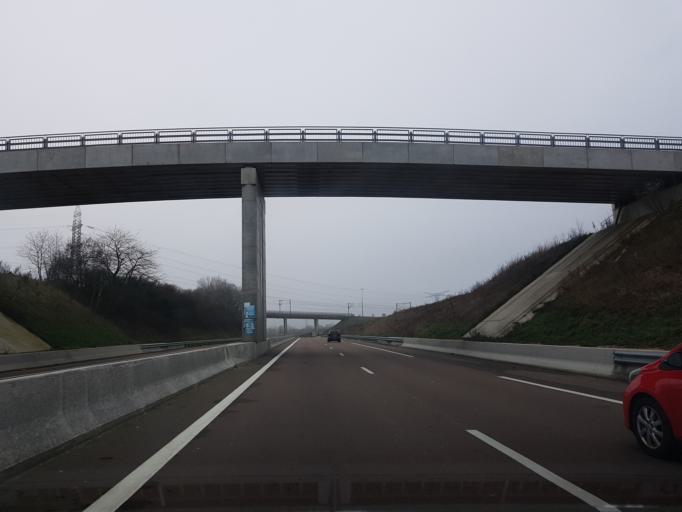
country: FR
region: Bourgogne
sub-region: Departement de Saone-et-Loire
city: Saint-Leu
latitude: 46.7487
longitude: 4.5085
